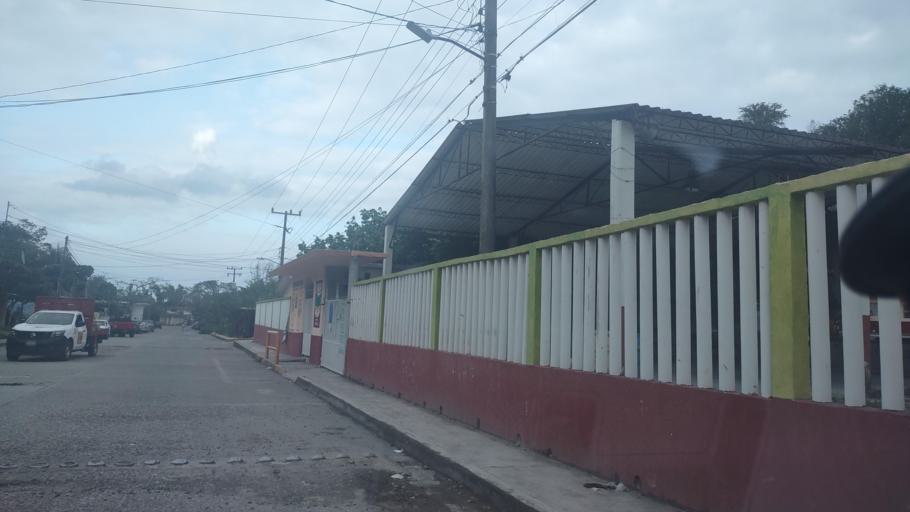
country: MX
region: Veracruz
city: Papantla de Olarte
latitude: 20.4516
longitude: -97.3126
